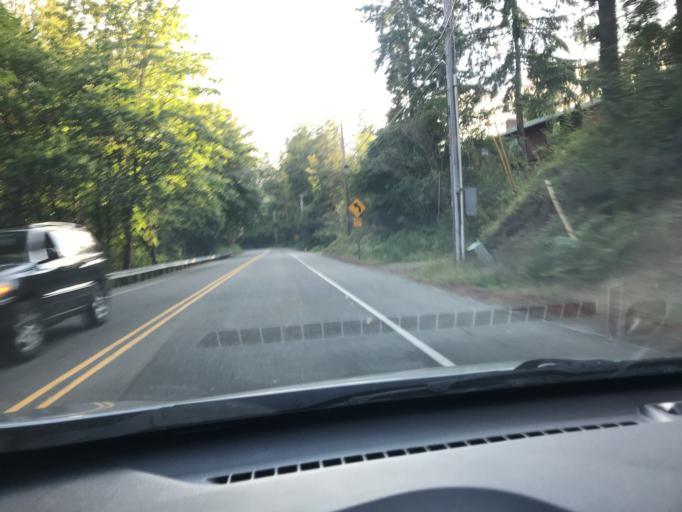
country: US
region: Washington
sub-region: King County
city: Black Diamond
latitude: 47.3109
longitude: -122.0403
